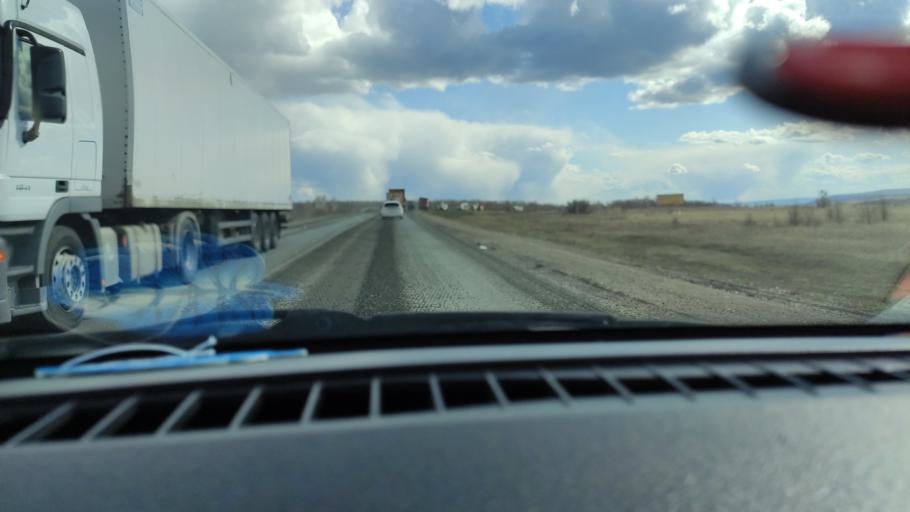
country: RU
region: Saratov
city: Dukhovnitskoye
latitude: 52.7141
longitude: 48.2667
